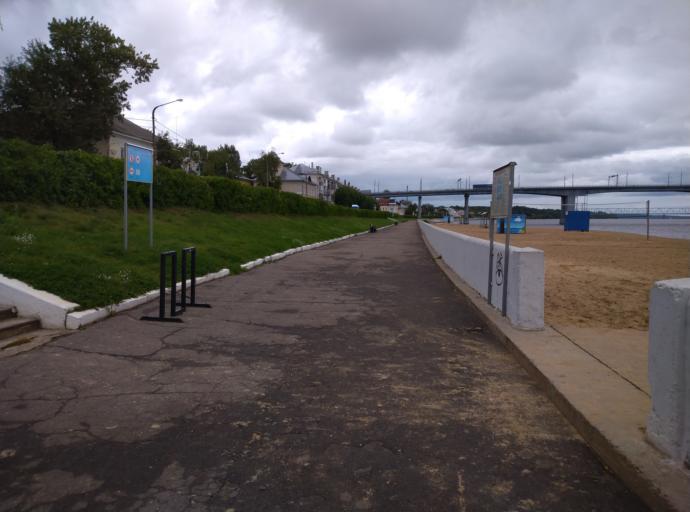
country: RU
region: Kostroma
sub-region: Kostromskoy Rayon
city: Kostroma
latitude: 57.7579
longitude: 40.9383
